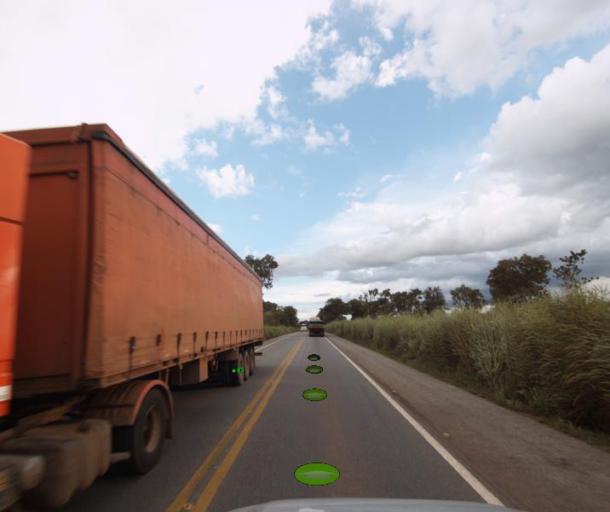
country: BR
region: Goias
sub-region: Porangatu
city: Porangatu
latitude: -13.3678
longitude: -49.1254
